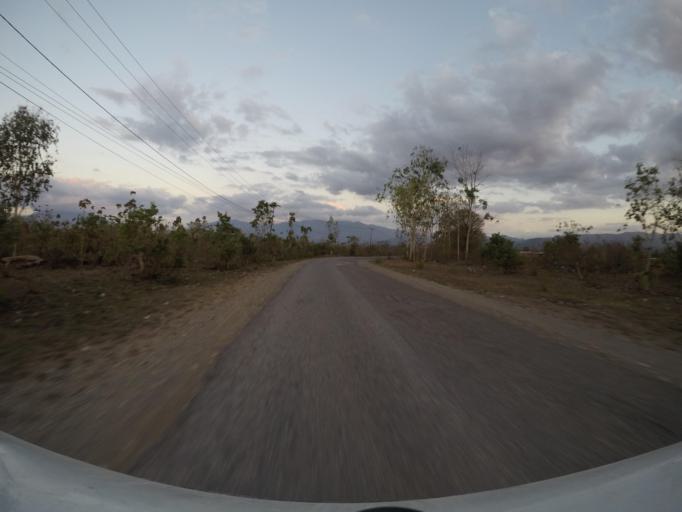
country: TL
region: Bobonaro
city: Maliana
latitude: -8.9656
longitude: 125.1277
